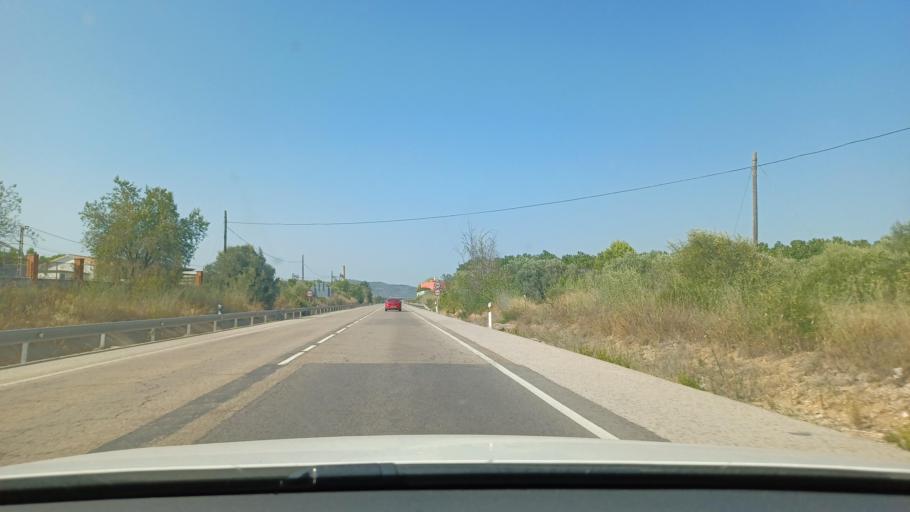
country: ES
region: Valencia
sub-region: Provincia de Castello
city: Alcala de Xivert
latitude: 40.3033
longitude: 0.2291
